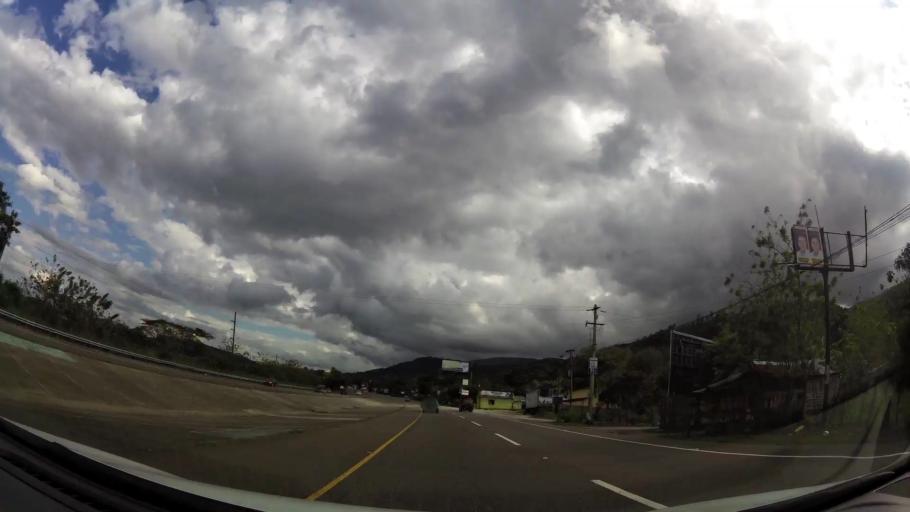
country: DO
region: La Vega
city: Concepcion de La Vega
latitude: 19.1573
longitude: -70.4834
